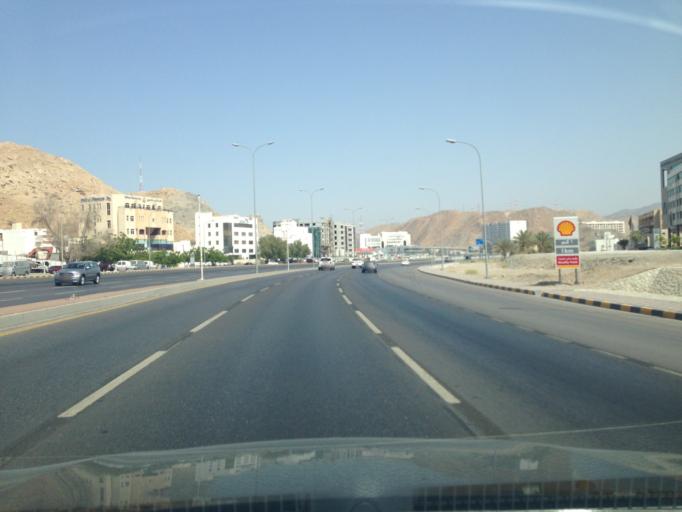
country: OM
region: Muhafazat Masqat
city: Muscat
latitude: 23.6000
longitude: 58.5182
